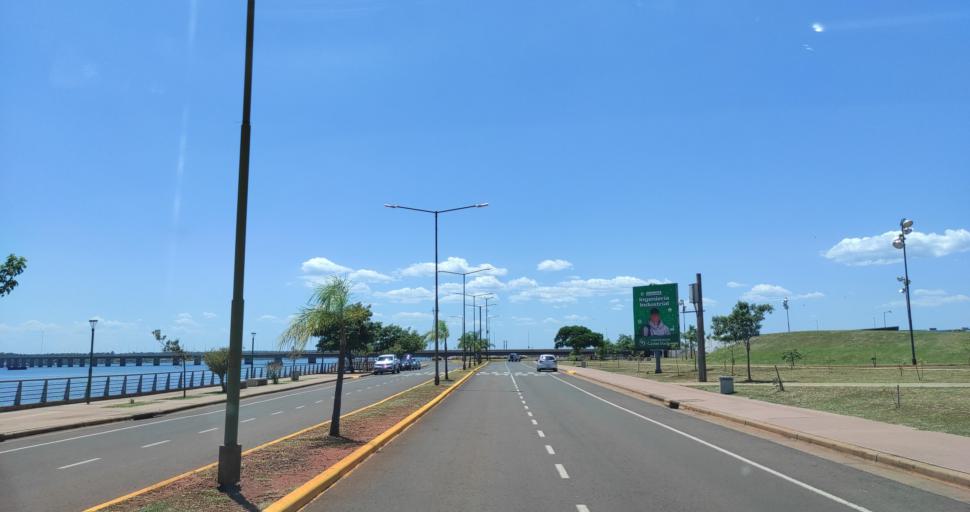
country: AR
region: Misiones
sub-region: Departamento de Capital
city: Posadas
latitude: -27.3741
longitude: -55.8819
